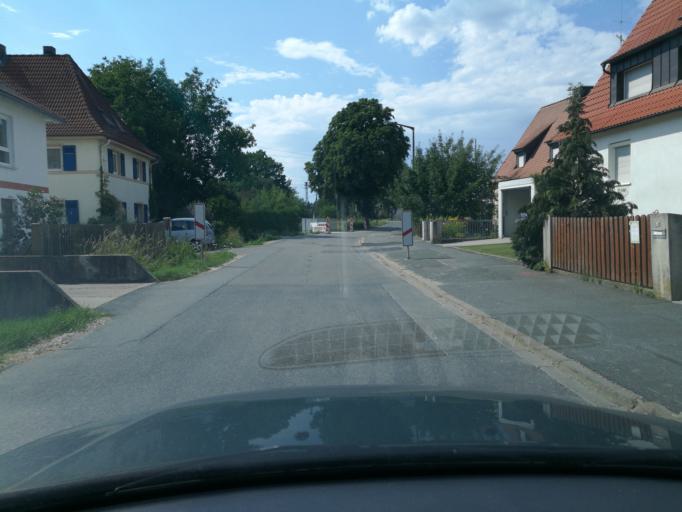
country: DE
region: Bavaria
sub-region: Regierungsbezirk Mittelfranken
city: Erlangen
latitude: 49.5351
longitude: 10.9983
